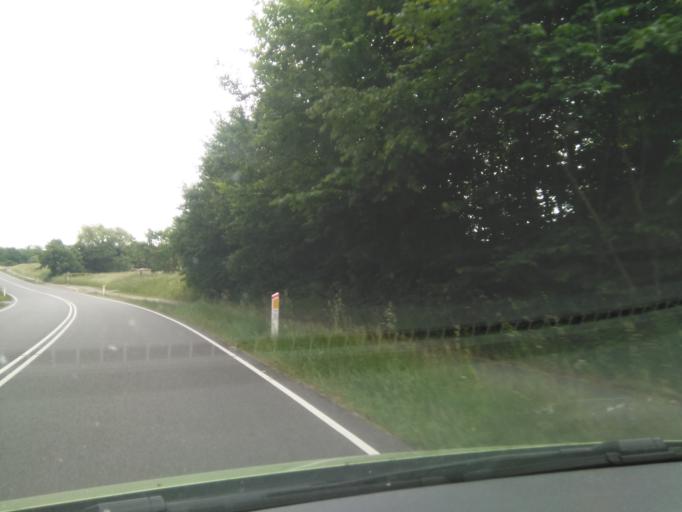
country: DK
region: Capital Region
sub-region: Bornholm Kommune
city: Akirkeby
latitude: 55.2346
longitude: 14.8749
